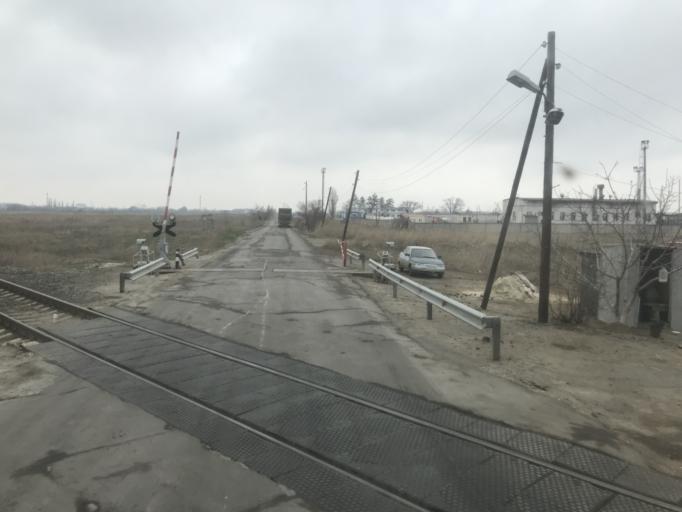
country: RU
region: Volgograd
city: Svetlyy Yar
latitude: 48.5141
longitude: 44.6336
